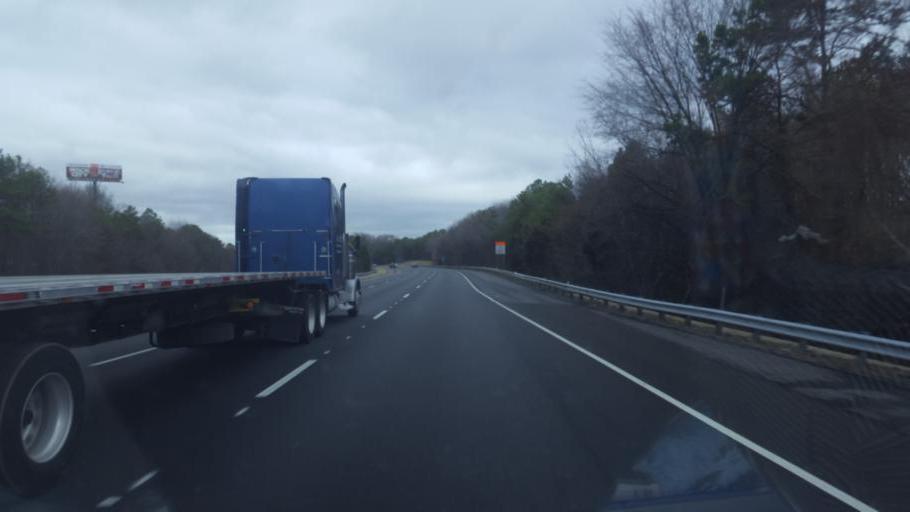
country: US
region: Georgia
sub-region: Catoosa County
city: Indian Springs
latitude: 34.9320
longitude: -85.1540
